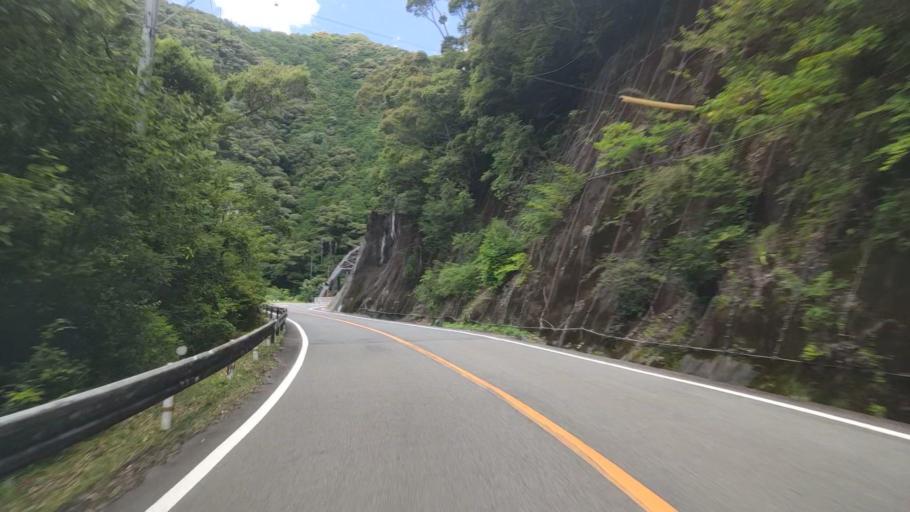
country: JP
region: Mie
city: Owase
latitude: 34.0014
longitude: 136.0093
